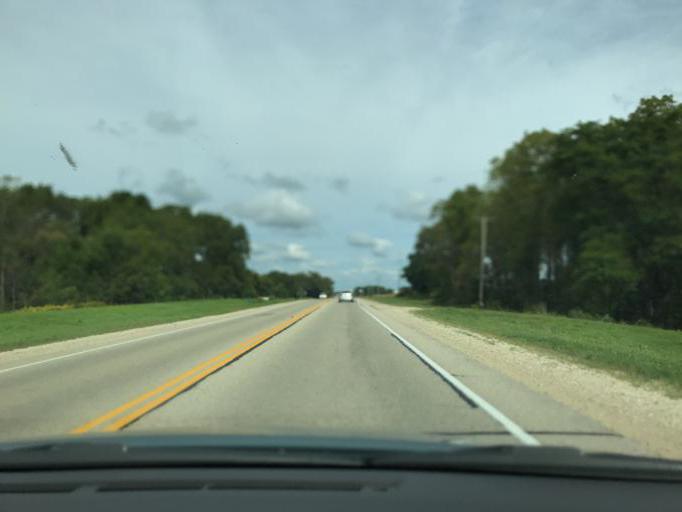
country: US
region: Wisconsin
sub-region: Racine County
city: Bohners Lake
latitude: 42.6431
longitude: -88.2514
